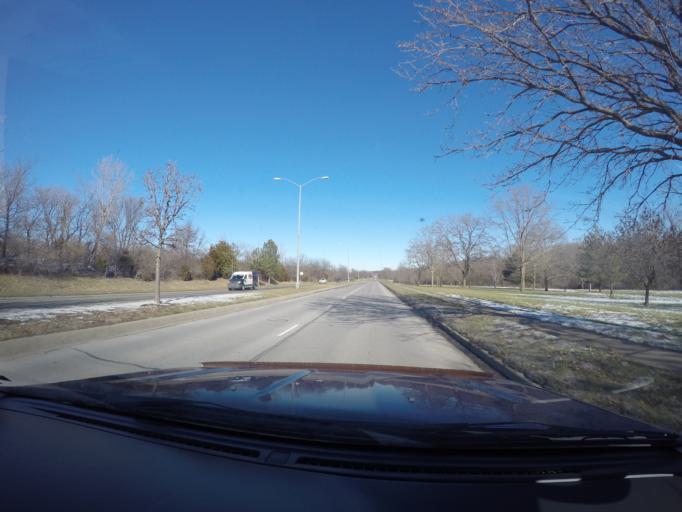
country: US
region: Kansas
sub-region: Johnson County
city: Olathe
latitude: 38.9034
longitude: -94.8151
